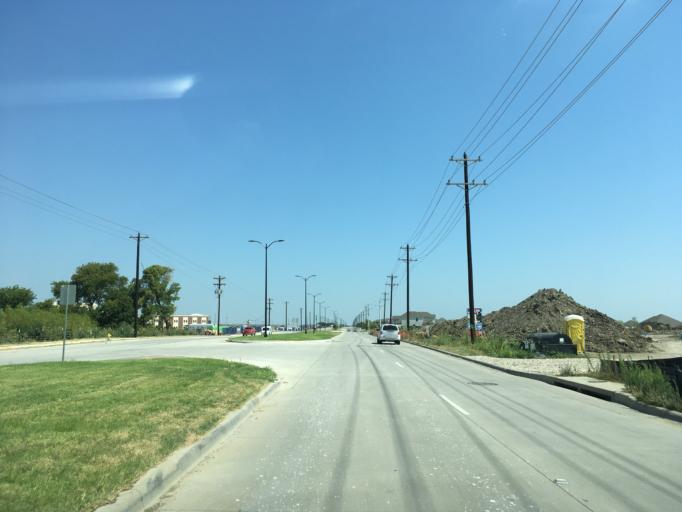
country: US
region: Texas
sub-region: Collin County
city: Prosper
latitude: 33.2050
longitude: -96.7676
